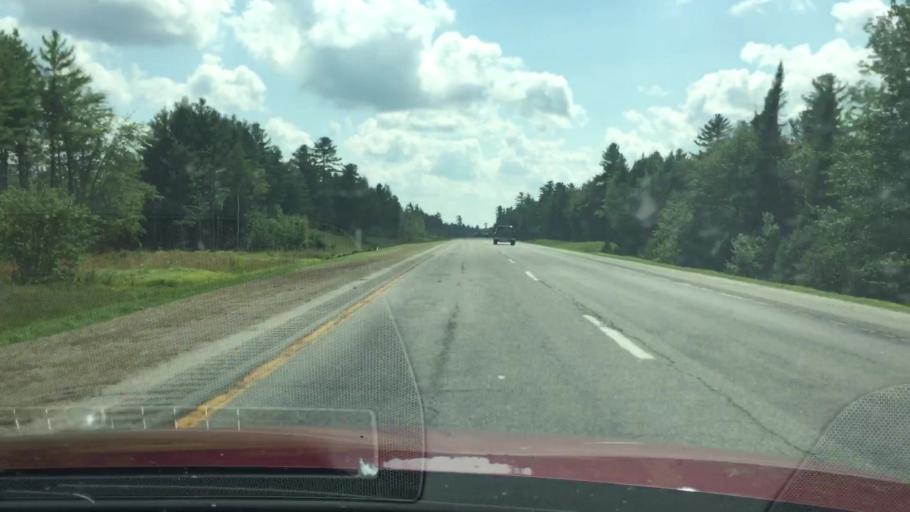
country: US
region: Maine
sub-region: Penobscot County
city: Medway
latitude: 45.5815
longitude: -68.5435
